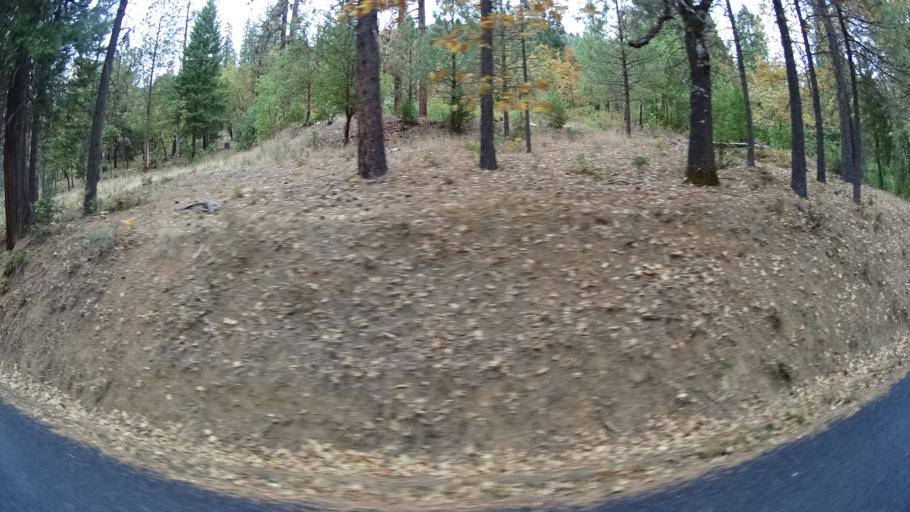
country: US
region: California
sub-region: Siskiyou County
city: Happy Camp
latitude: 41.8592
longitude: -123.1601
